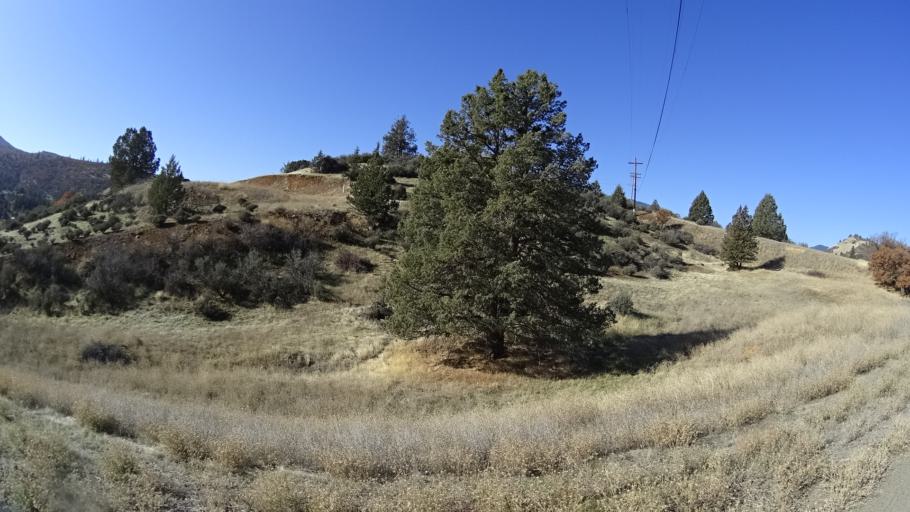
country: US
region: California
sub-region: Siskiyou County
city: Montague
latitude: 41.8993
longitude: -122.5229
